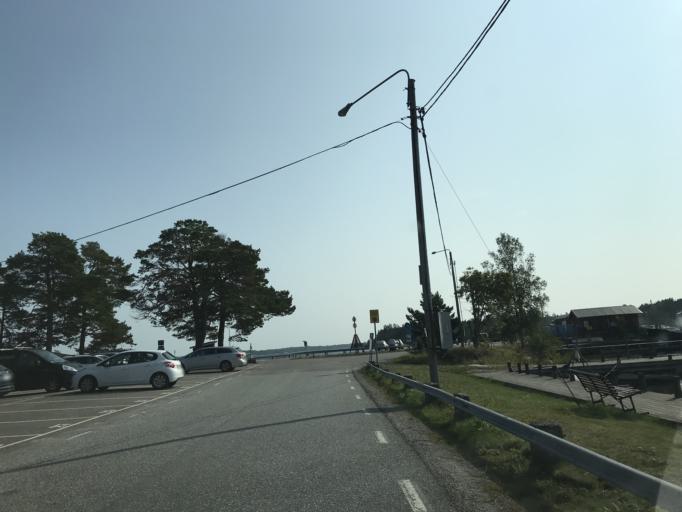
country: SE
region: Stockholm
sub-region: Norrtalje Kommun
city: Bjorko
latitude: 59.8707
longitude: 19.0774
